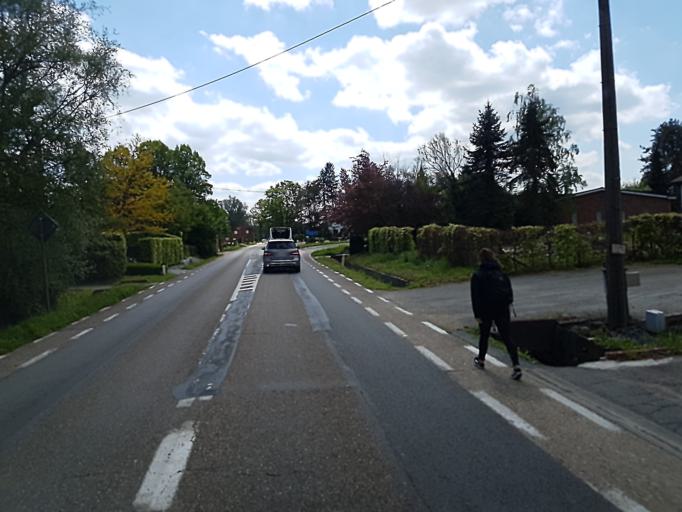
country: BE
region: Flanders
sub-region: Provincie Antwerpen
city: Laakdal
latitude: 51.0600
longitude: 4.9948
